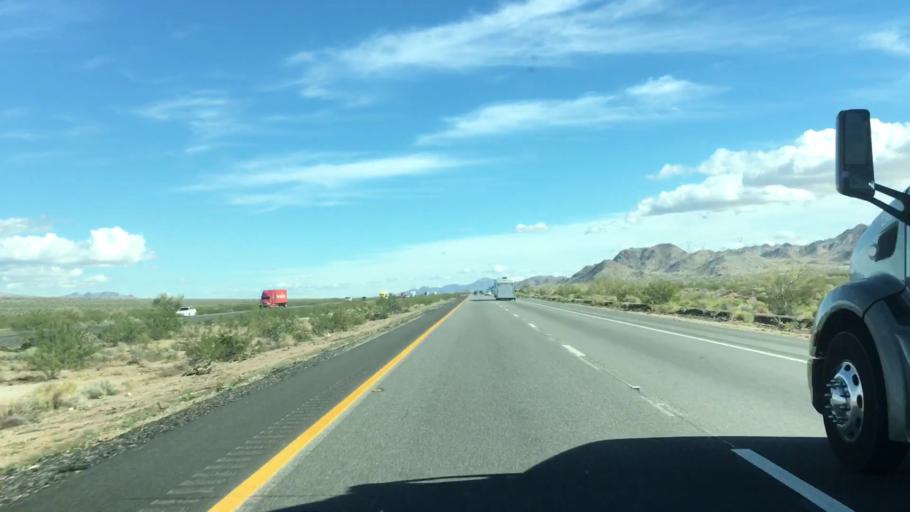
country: US
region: California
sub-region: Riverside County
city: Mecca
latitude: 33.6595
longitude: -115.7519
